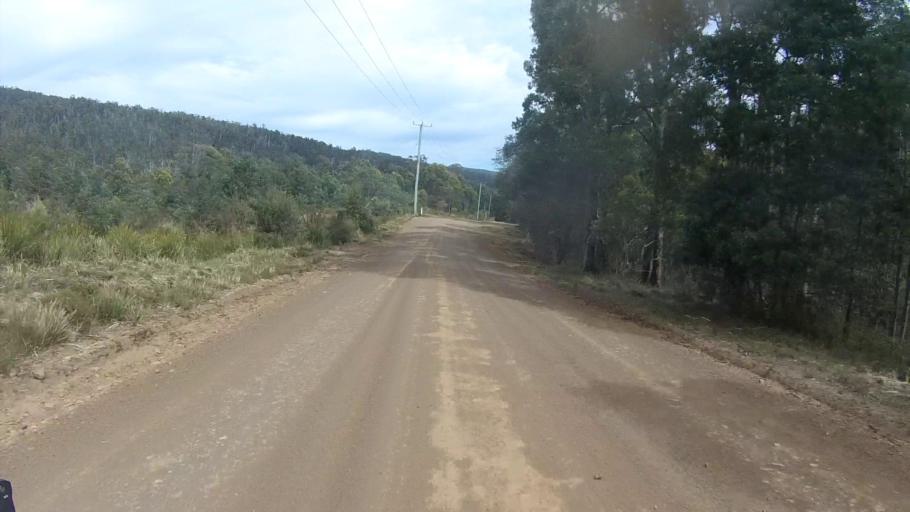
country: AU
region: Tasmania
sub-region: Sorell
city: Sorell
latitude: -42.7532
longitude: 147.7985
